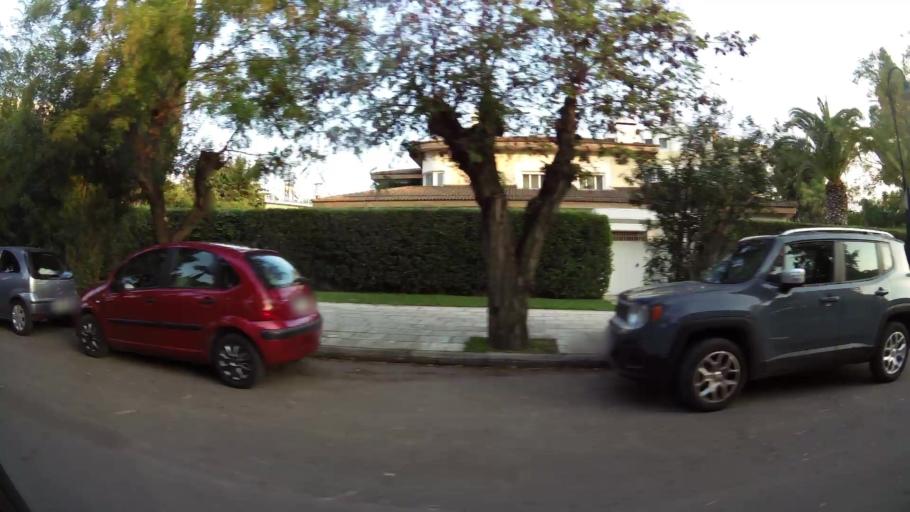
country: GR
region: Attica
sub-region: Nomarchia Athinas
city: Psychiko
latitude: 38.0129
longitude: 23.7725
